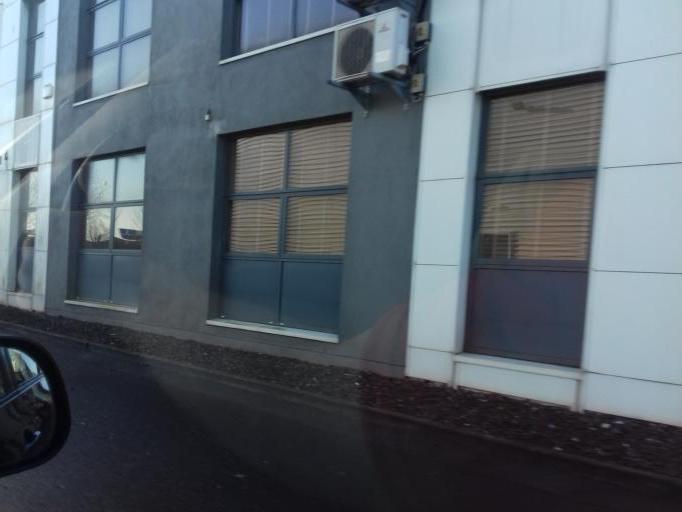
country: IE
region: Leinster
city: Beaumont
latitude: 53.4090
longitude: -6.2350
